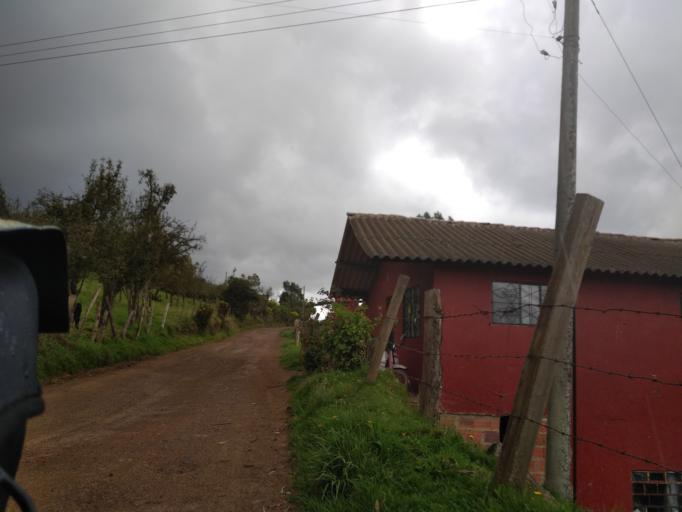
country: CO
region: Boyaca
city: Sotaquira
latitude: 5.7659
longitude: -73.2679
